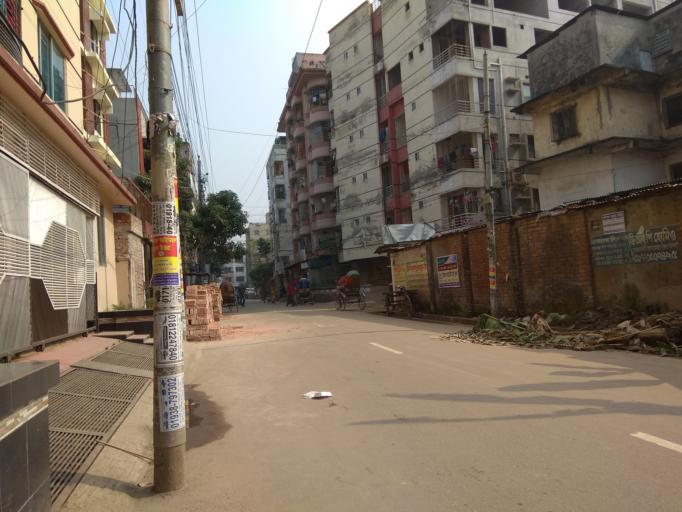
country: BD
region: Dhaka
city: Tungi
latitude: 23.8635
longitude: 90.3887
